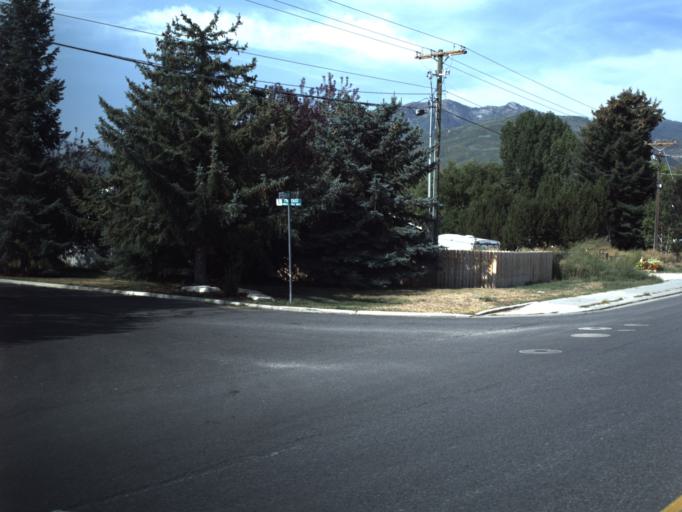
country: US
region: Utah
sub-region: Wasatch County
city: Midway
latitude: 40.5117
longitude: -111.4556
